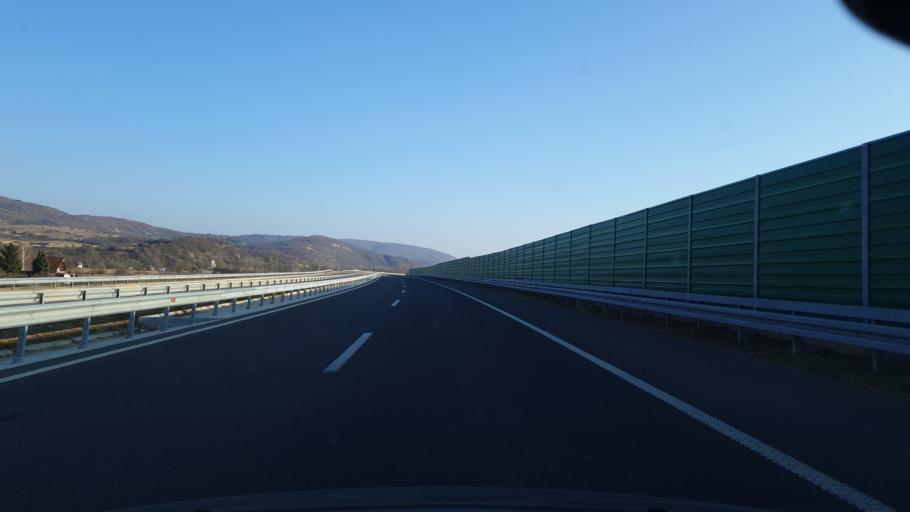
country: RS
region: Central Serbia
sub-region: Pirotski Okrug
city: Pirot
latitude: 43.0740
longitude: 22.6711
